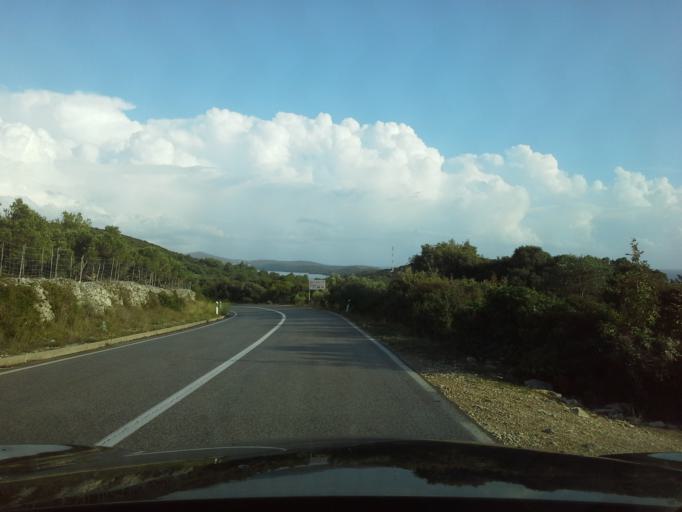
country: HR
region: Primorsko-Goranska
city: Mali Losinj
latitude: 44.5809
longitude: 14.4132
